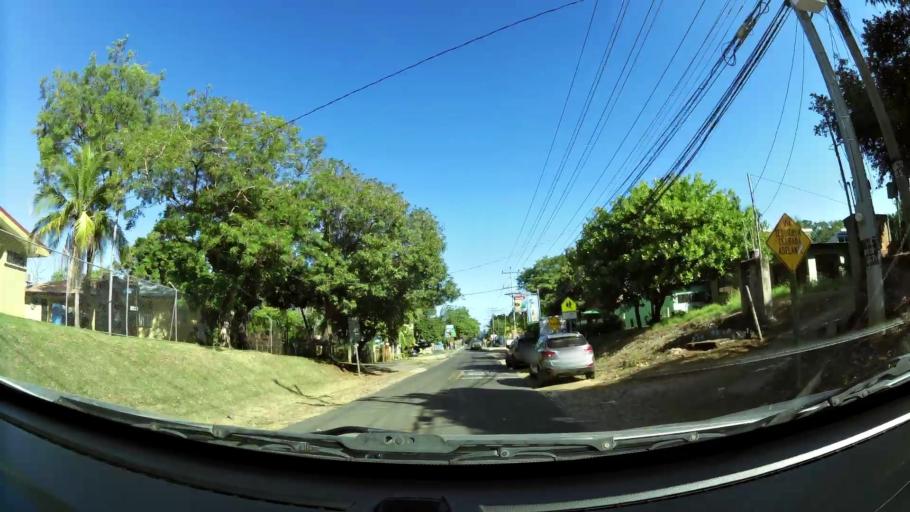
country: CR
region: Guanacaste
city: Sardinal
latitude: 10.4062
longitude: -85.7966
